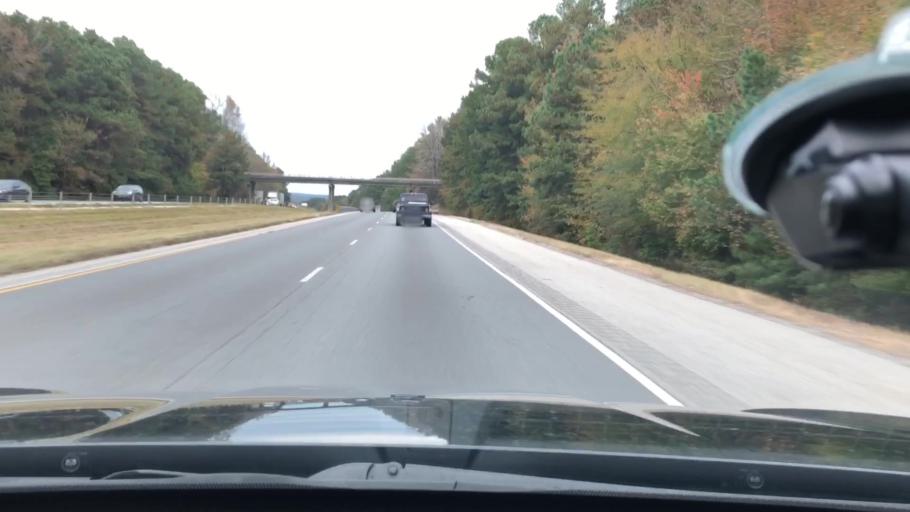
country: US
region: Arkansas
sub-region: Clark County
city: Arkadelphia
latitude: 34.1409
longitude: -93.0809
